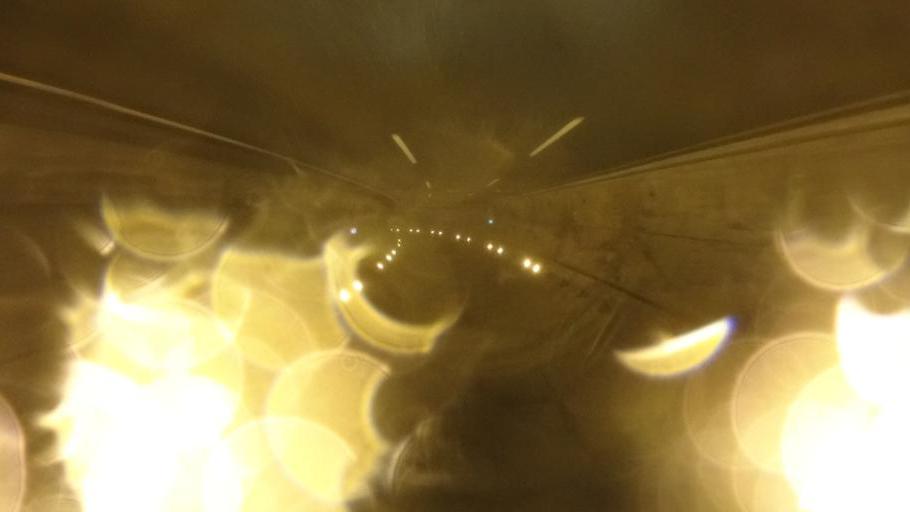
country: ES
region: Galicia
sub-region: Provincia de Lugo
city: Becerrea
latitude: 42.8699
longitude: -7.1749
